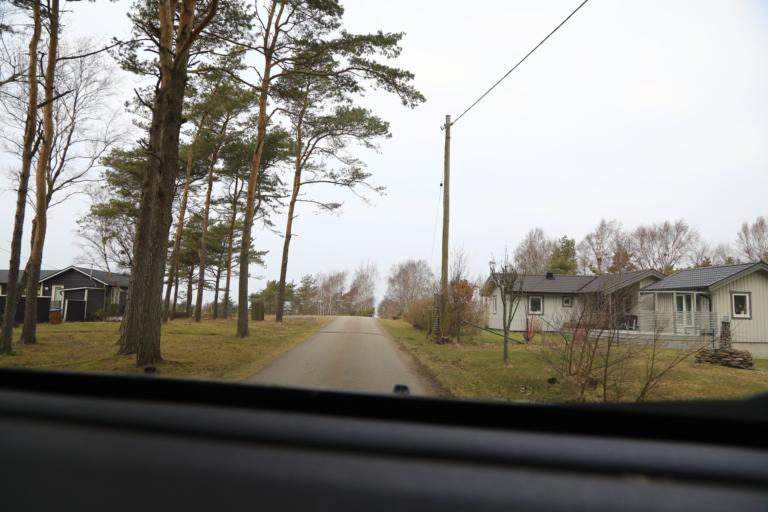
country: SE
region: Halland
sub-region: Kungsbacka Kommun
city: Frillesas
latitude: 57.2668
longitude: 12.1185
